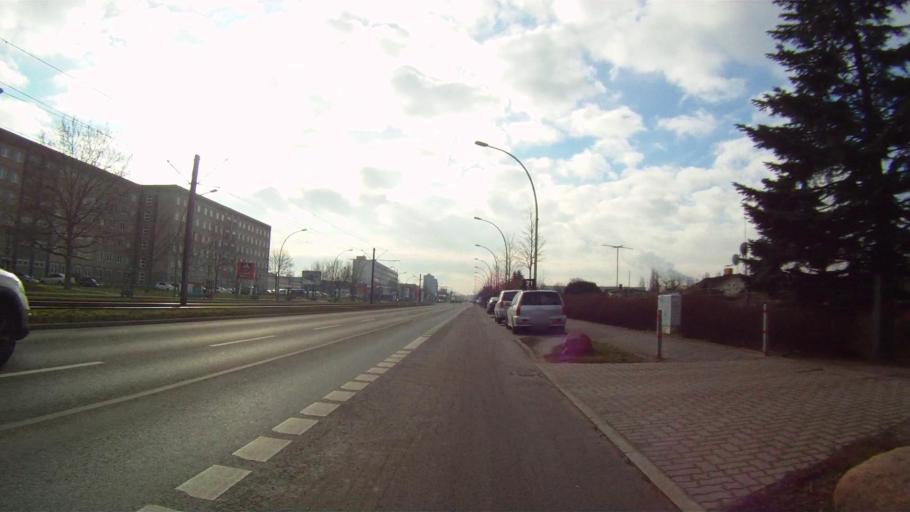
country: DE
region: Berlin
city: Friedrichsfelde
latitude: 52.5210
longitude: 13.5193
